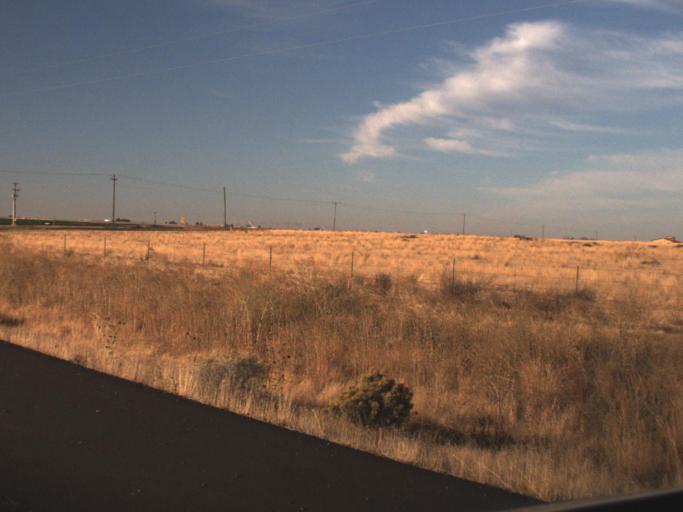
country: US
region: Washington
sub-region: Franklin County
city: Connell
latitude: 46.7219
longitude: -118.8339
